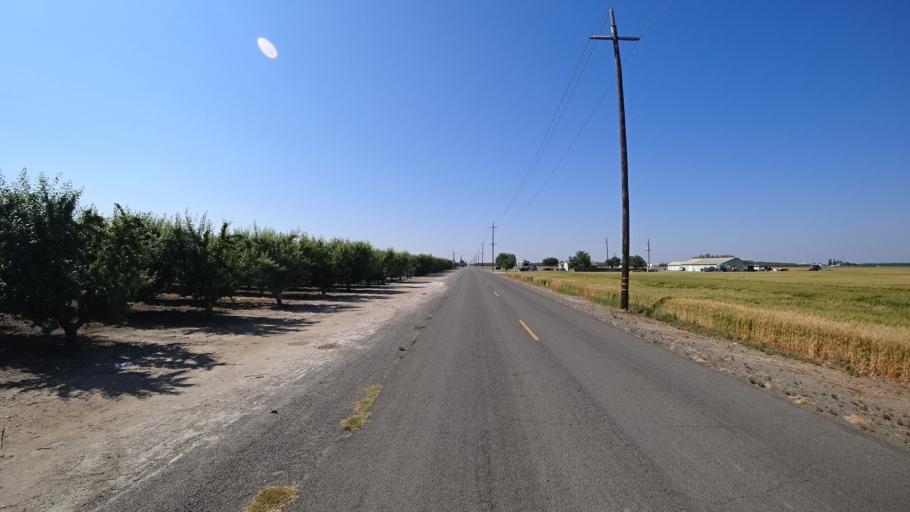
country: US
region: California
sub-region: Kings County
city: Lucerne
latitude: 36.3925
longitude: -119.5830
